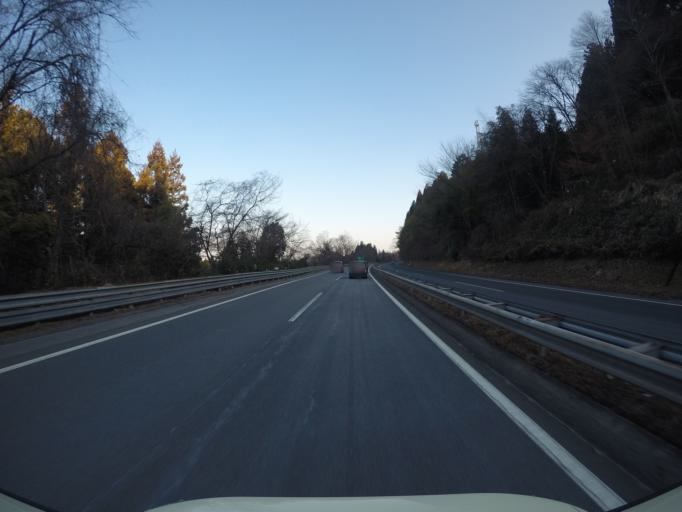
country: JP
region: Tochigi
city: Nikko
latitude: 36.7361
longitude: 139.6422
